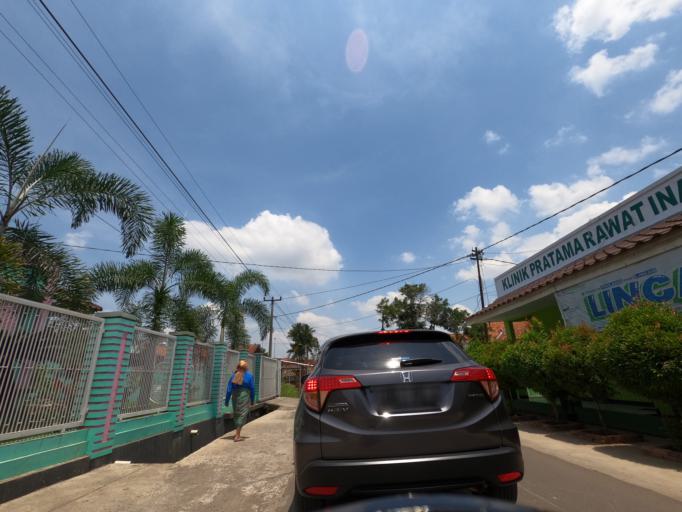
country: ID
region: West Java
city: Pamanukan
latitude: -6.5322
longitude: 107.7717
